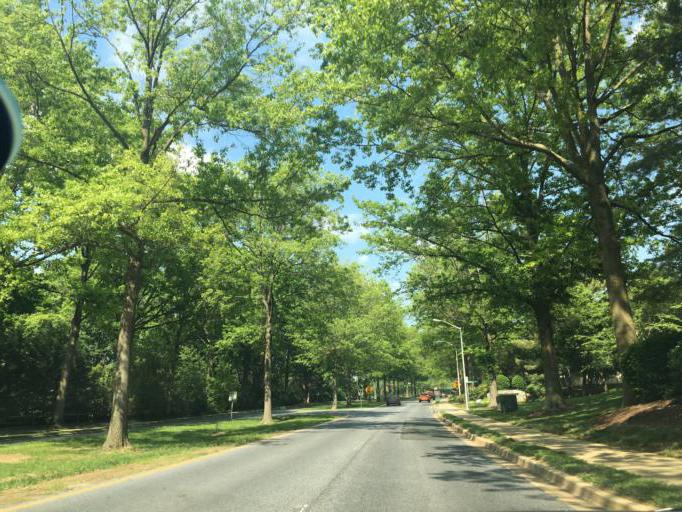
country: US
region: Maryland
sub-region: Montgomery County
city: Montgomery Village
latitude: 39.1896
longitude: -77.1945
